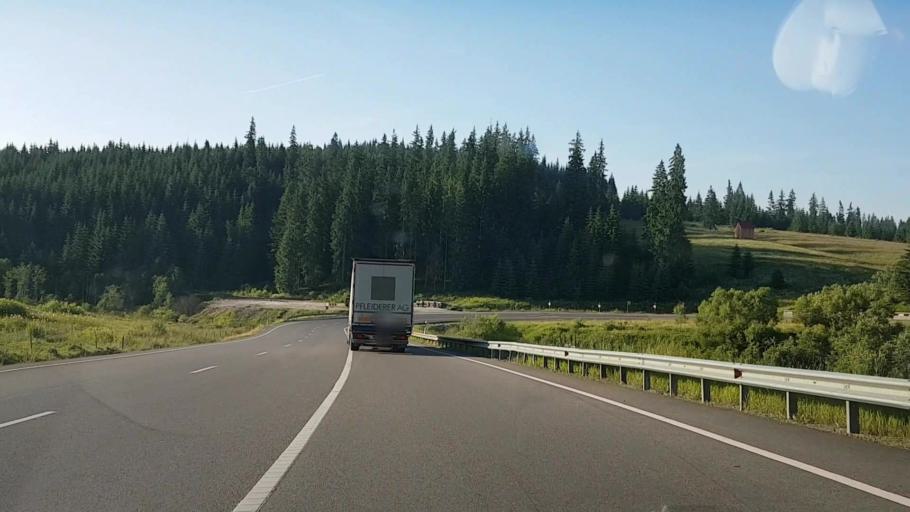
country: RO
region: Suceava
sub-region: Comuna Poiana Stampei
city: Poiana Stampei
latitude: 47.2987
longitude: 25.0959
